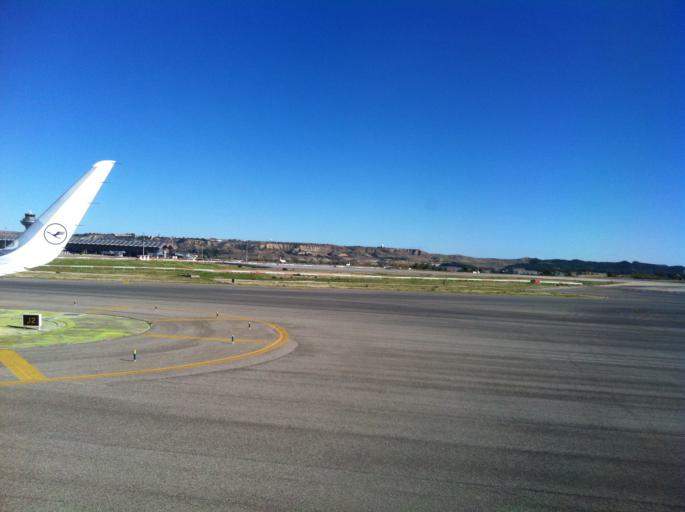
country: ES
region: Madrid
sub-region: Provincia de Madrid
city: Barajas de Madrid
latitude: 40.4853
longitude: -3.5800
